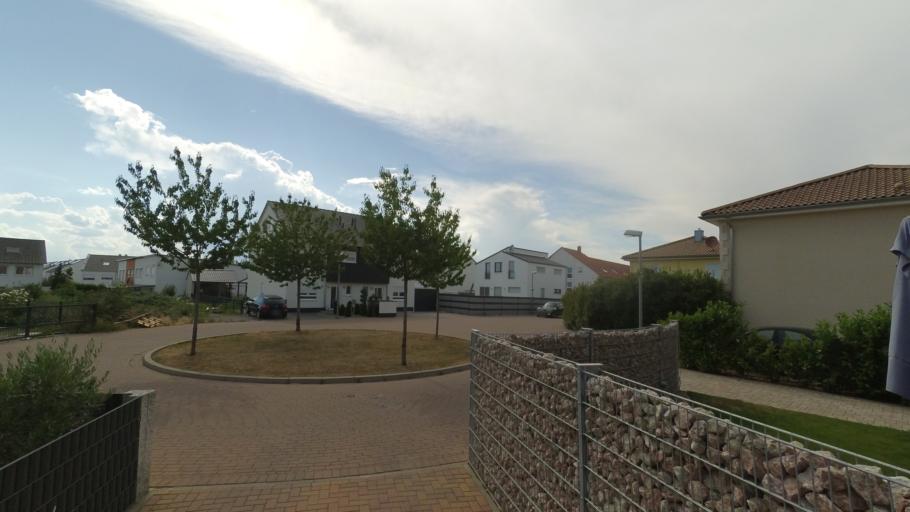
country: DE
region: Rheinland-Pfalz
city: Frankenthal
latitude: 49.5083
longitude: 8.3862
